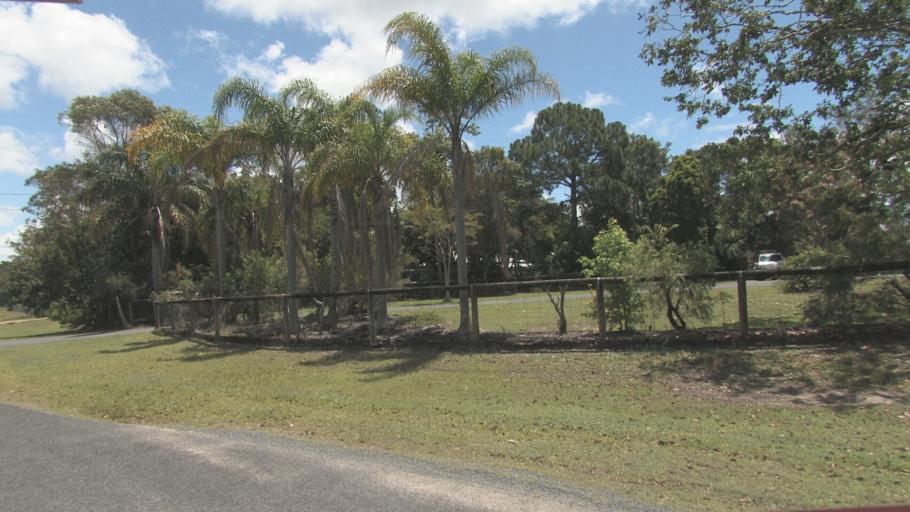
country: AU
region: Queensland
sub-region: Redland
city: Redland Bay
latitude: -27.6793
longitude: 153.2788
